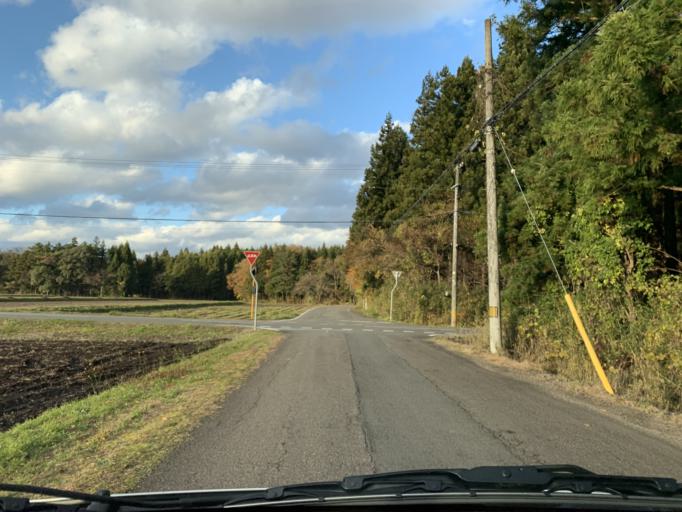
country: JP
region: Iwate
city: Mizusawa
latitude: 39.1197
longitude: 141.0271
